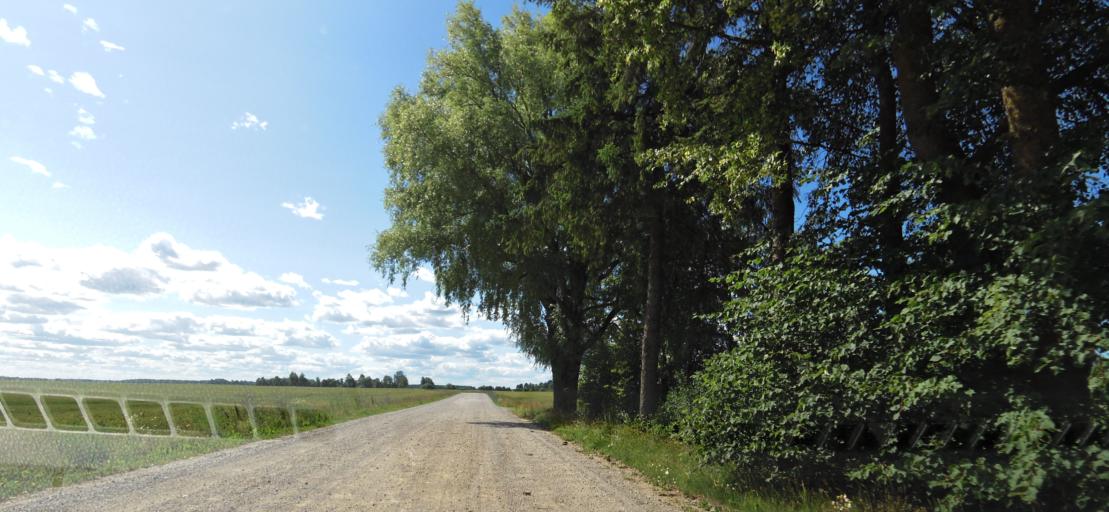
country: LV
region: Bauskas Rajons
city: Bauska
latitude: 56.2400
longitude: 24.2127
